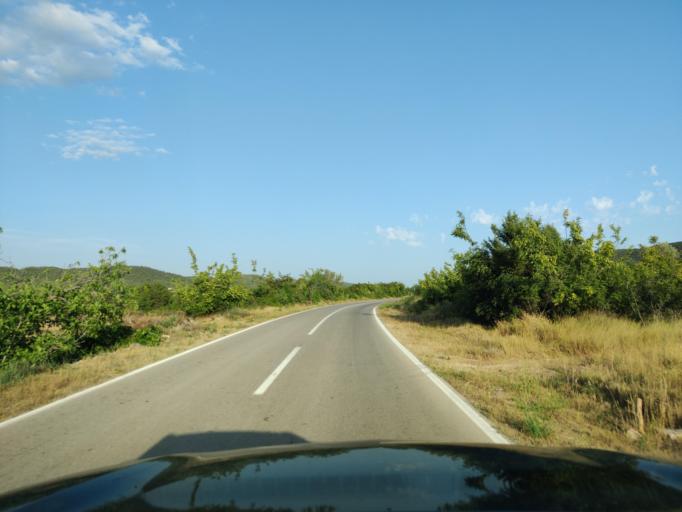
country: HR
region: Sibensko-Kniniska
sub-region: Grad Sibenik
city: Pirovac
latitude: 43.7922
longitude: 15.6919
